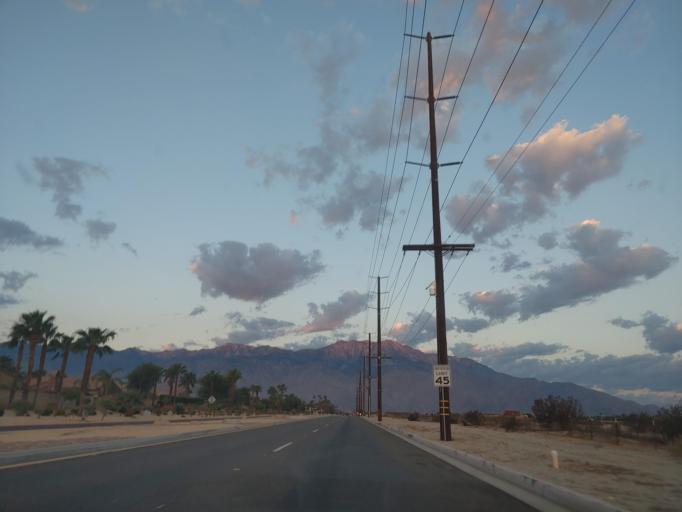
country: US
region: California
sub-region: Riverside County
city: Cathedral City
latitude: 33.8016
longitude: -116.4421
